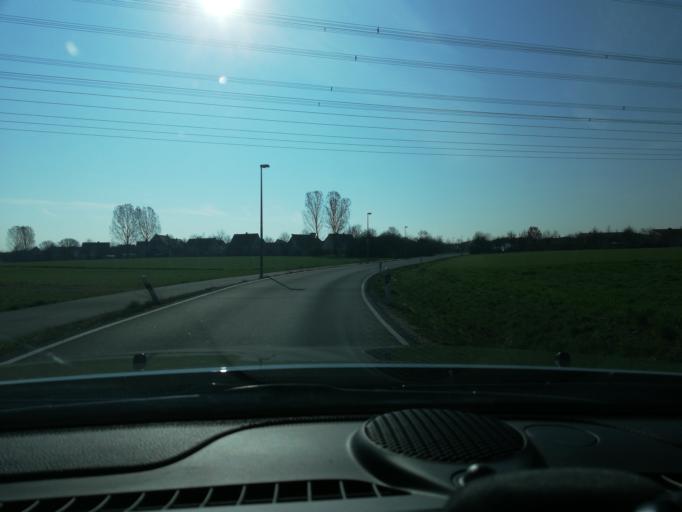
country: DE
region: Bavaria
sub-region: Regierungsbezirk Mittelfranken
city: Hessdorf
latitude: 49.5997
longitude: 10.9434
